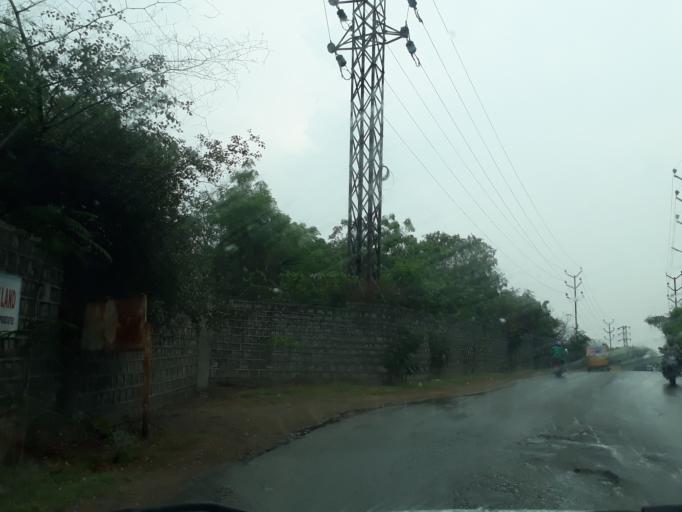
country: IN
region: Telangana
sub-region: Hyderabad
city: Malkajgiri
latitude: 17.4689
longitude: 78.5034
